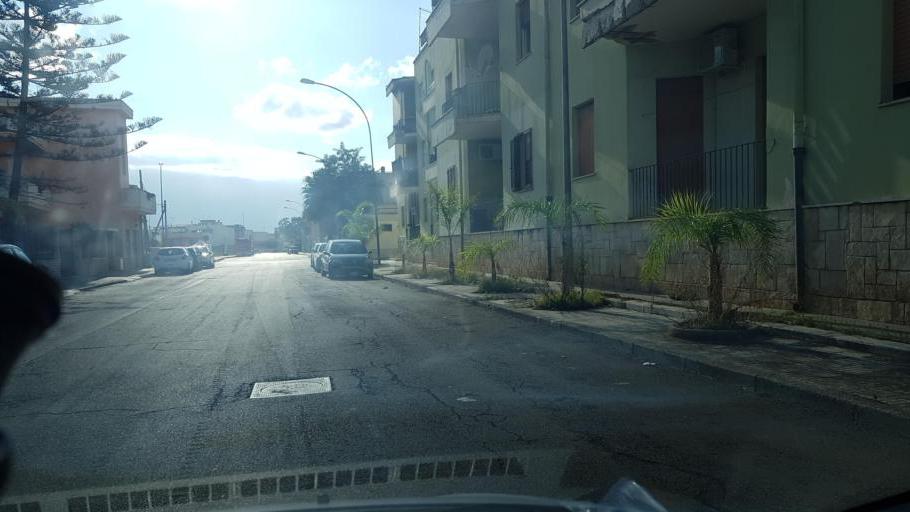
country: IT
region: Apulia
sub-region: Provincia di Lecce
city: Squinzano
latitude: 40.4372
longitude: 18.0346
